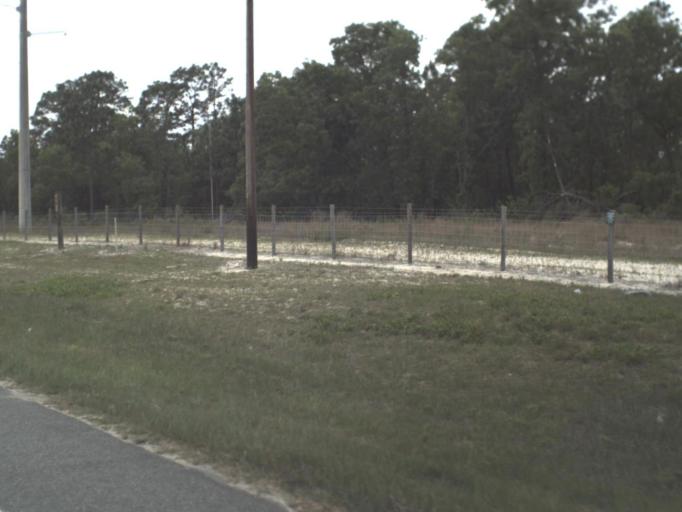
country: US
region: Florida
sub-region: Clay County
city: Keystone Heights
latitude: 29.8168
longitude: -81.9999
